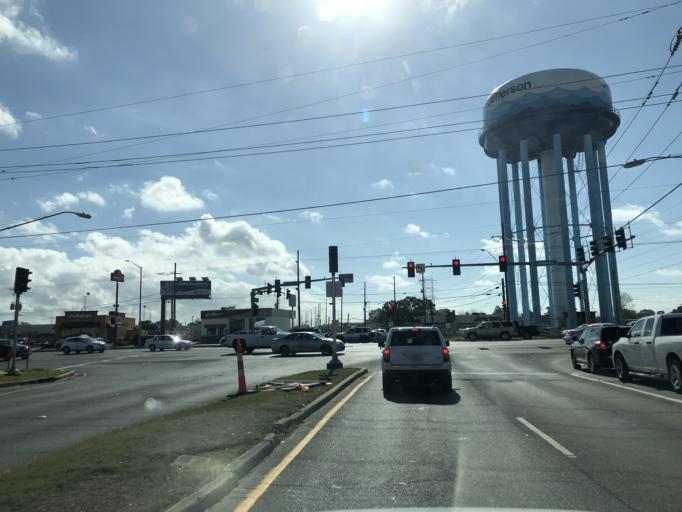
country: US
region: Louisiana
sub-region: Jefferson Parish
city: Kenner
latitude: 30.0058
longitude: -90.2209
